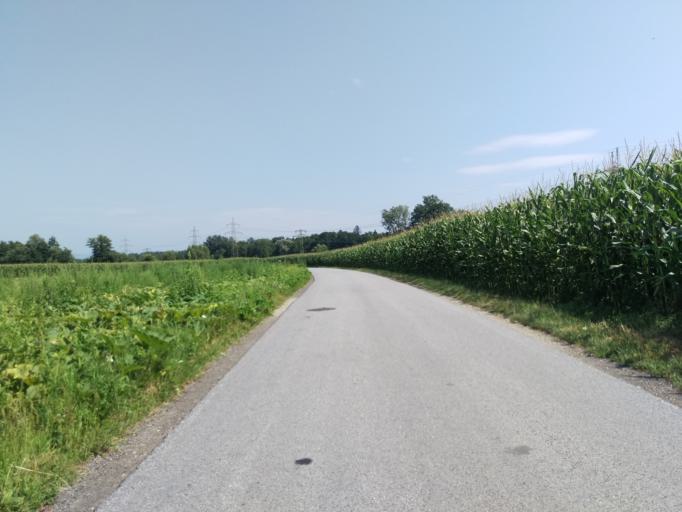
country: AT
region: Styria
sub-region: Politischer Bezirk Graz-Umgebung
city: Kalsdorf bei Graz
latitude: 46.9493
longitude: 15.4898
